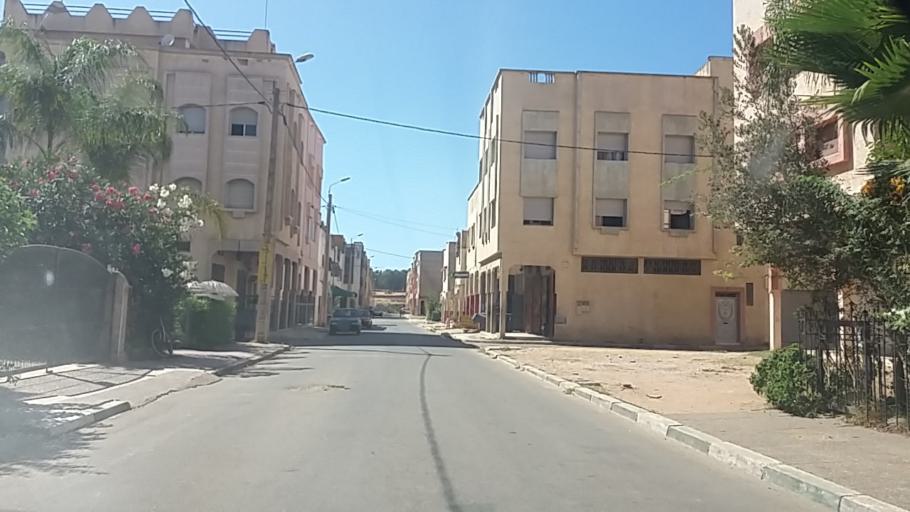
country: MA
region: Gharb-Chrarda-Beni Hssen
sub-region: Kenitra Province
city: Kenitra
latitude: 34.2387
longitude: -6.6179
